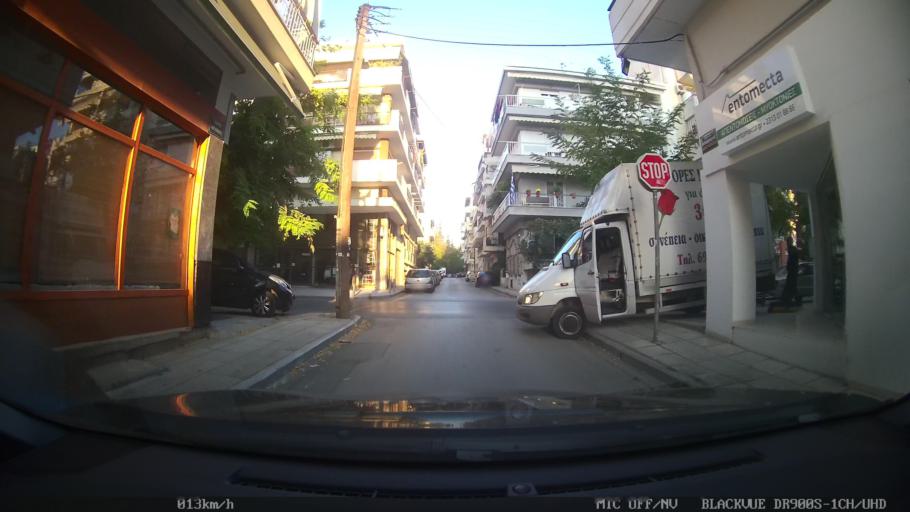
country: GR
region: Central Macedonia
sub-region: Nomos Thessalonikis
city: Triandria
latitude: 40.6037
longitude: 22.9712
